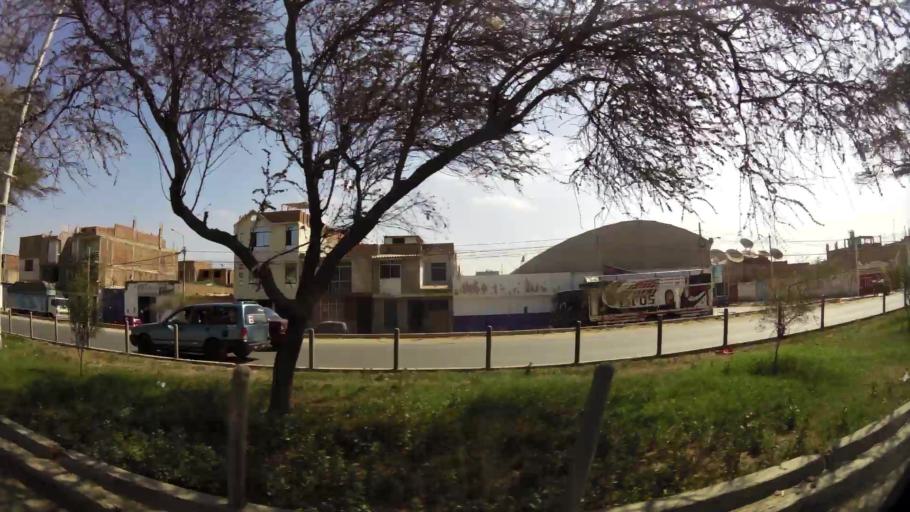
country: PE
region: Lambayeque
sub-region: Provincia de Chiclayo
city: Chiclayo
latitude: -6.7901
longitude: -79.8323
